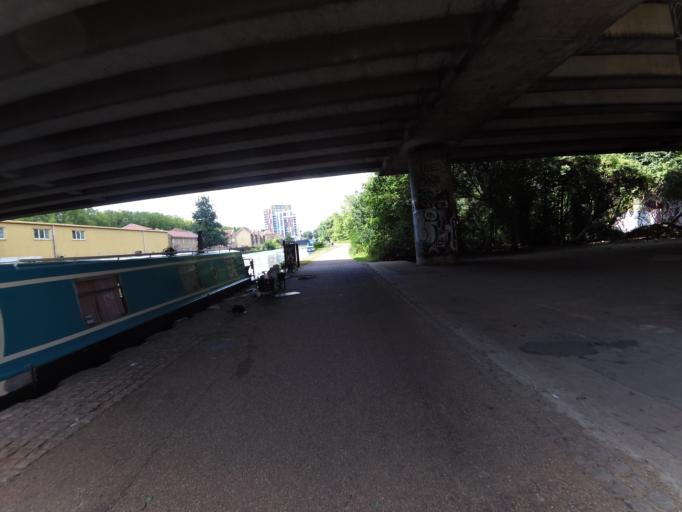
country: GB
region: England
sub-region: Greater London
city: Hackney
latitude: 51.5485
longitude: -0.0268
